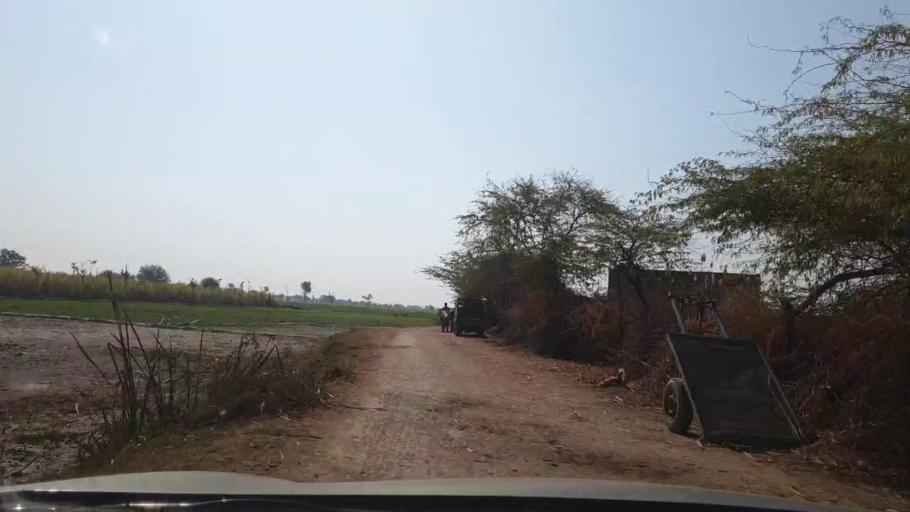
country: PK
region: Sindh
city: Berani
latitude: 25.6456
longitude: 68.8935
